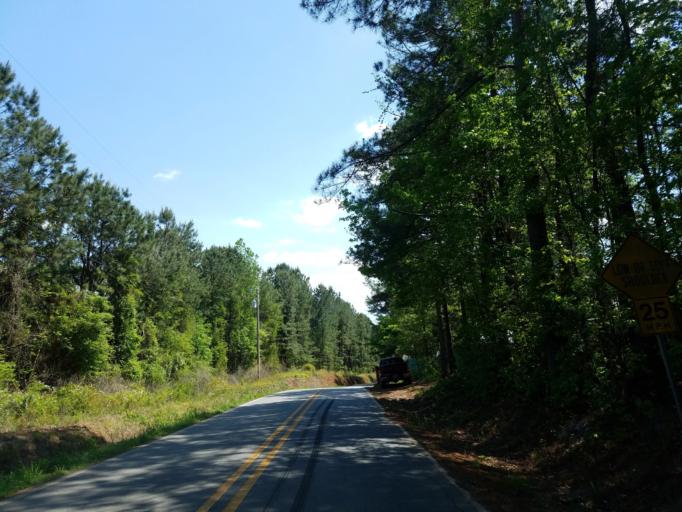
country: US
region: Georgia
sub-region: Butts County
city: Indian Springs
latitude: 33.1663
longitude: -84.0181
